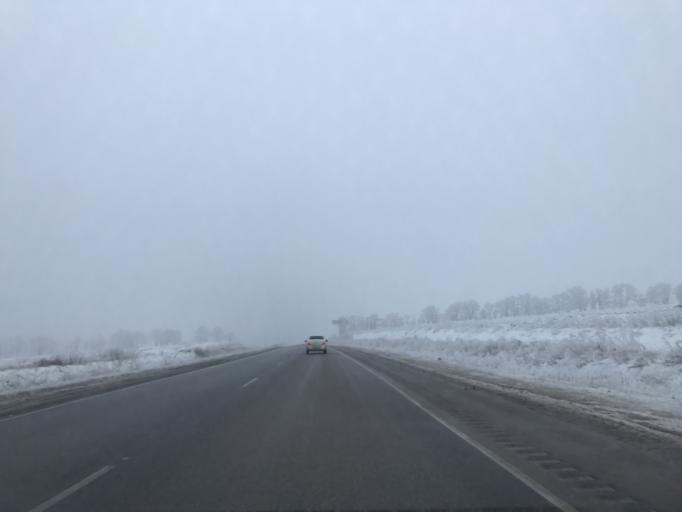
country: RU
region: Rostov
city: Severnyy
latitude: 47.3668
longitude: 39.6992
